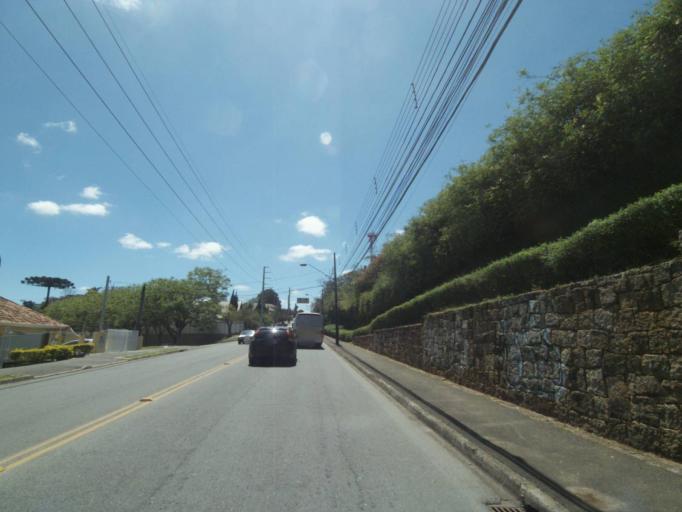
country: BR
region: Parana
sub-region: Curitiba
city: Curitiba
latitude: -25.3912
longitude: -49.2724
